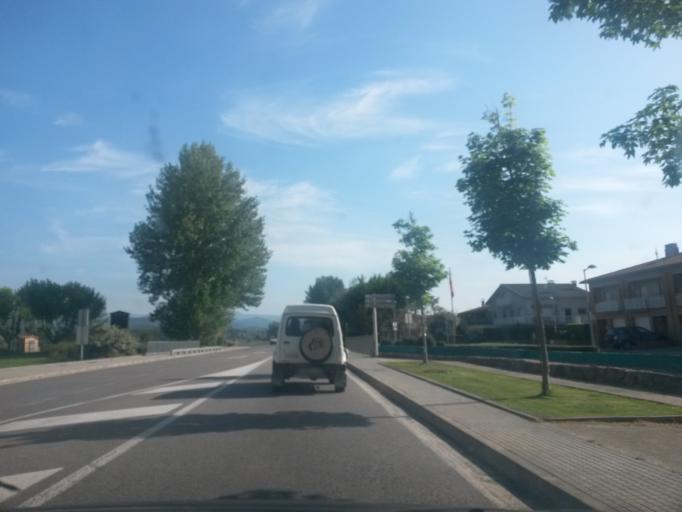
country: ES
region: Catalonia
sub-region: Provincia de Girona
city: Bas
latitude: 42.1479
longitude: 2.4607
